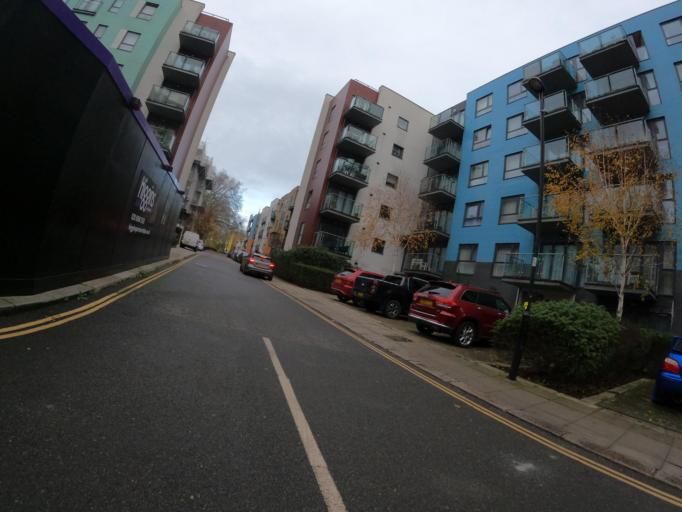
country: GB
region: England
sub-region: Greater London
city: Acton
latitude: 51.4999
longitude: -0.2706
